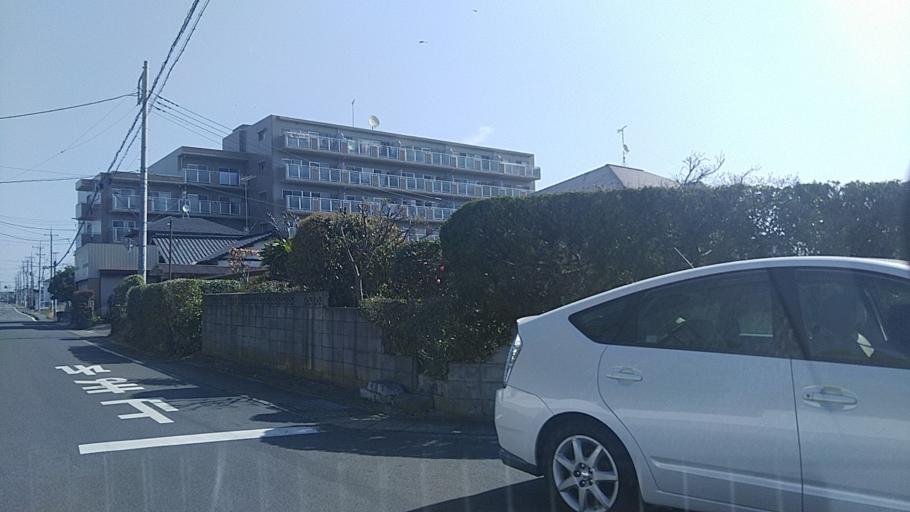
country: JP
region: Ibaraki
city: Ryugasaki
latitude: 35.8520
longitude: 140.1457
